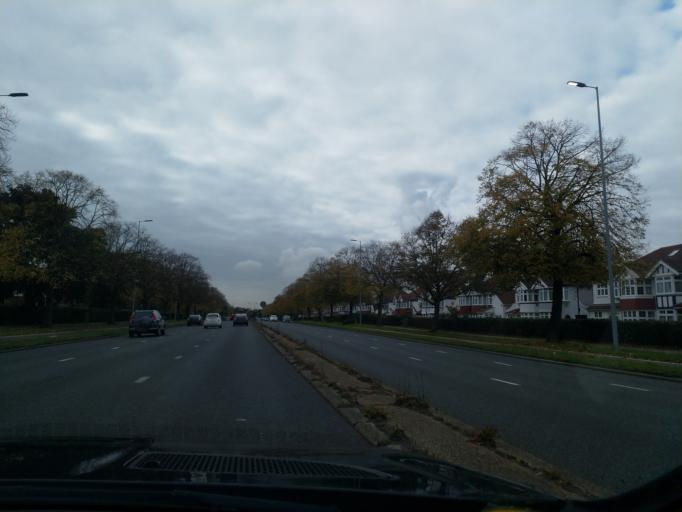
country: GB
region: England
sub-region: Greater London
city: Hounslow
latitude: 51.4760
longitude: -0.3874
